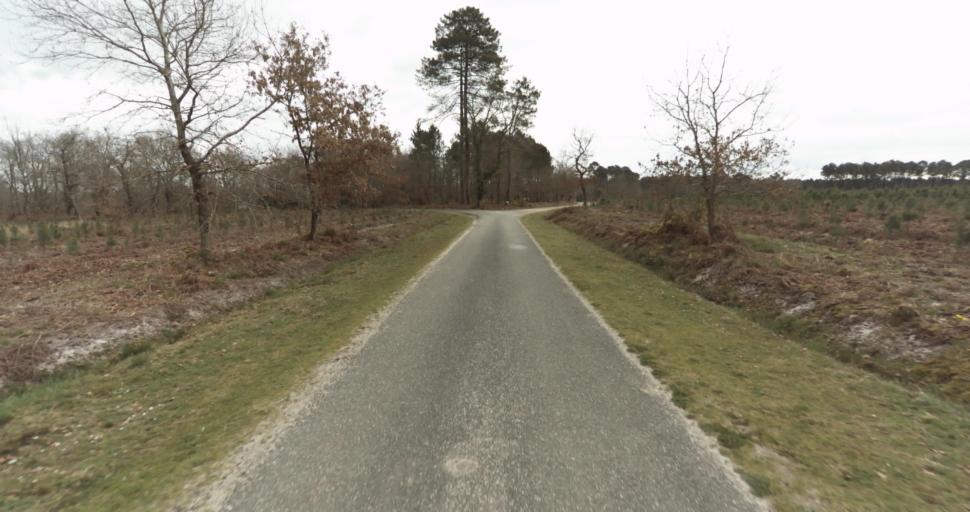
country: FR
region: Aquitaine
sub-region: Departement des Landes
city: Sarbazan
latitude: 44.0143
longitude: -0.2951
